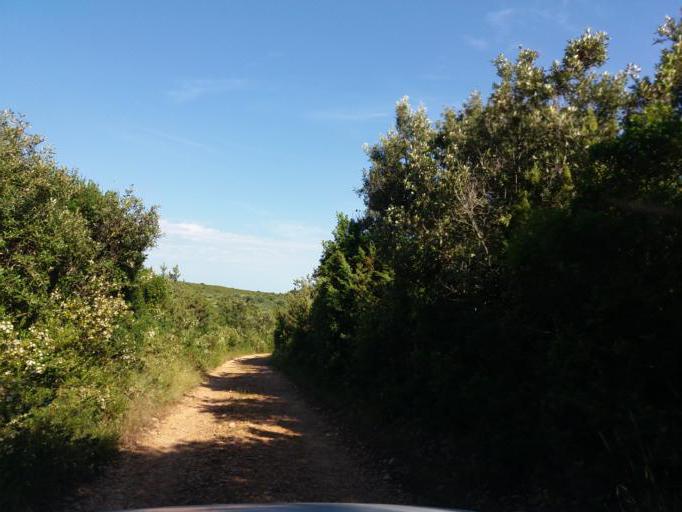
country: HR
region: Zadarska
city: Ugljan
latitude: 44.1314
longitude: 14.8628
